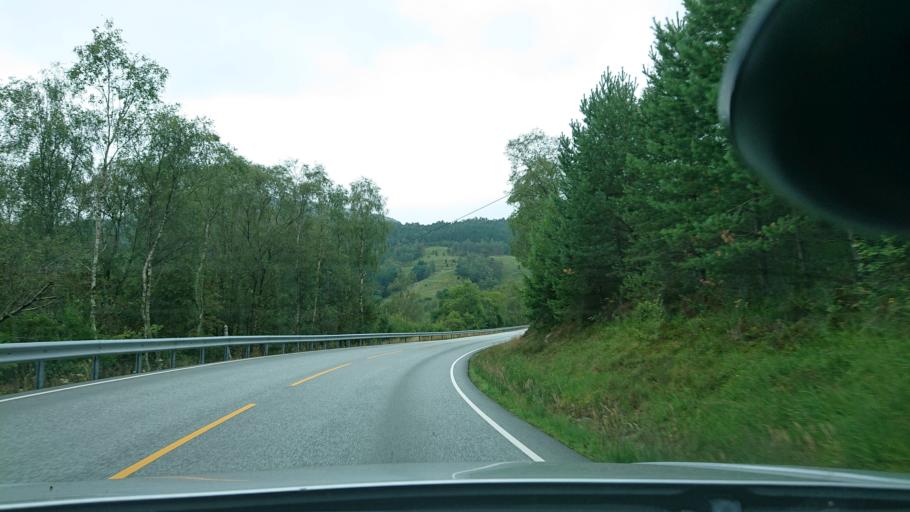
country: NO
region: Rogaland
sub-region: Hjelmeland
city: Hjelmelandsvagen
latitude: 59.1653
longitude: 6.1540
